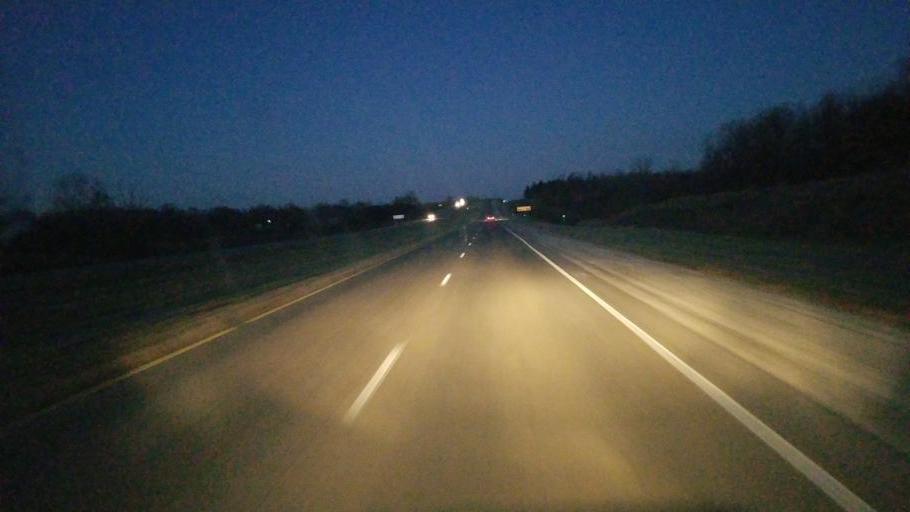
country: US
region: Iowa
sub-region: Des Moines County
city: West Burlington
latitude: 40.8328
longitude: -91.2511
